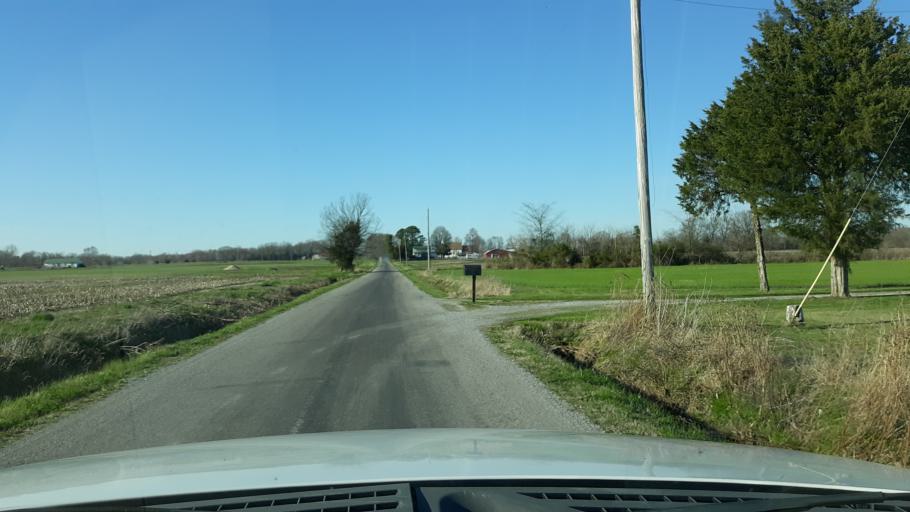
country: US
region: Illinois
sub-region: Saline County
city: Harrisburg
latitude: 37.8003
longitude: -88.6055
